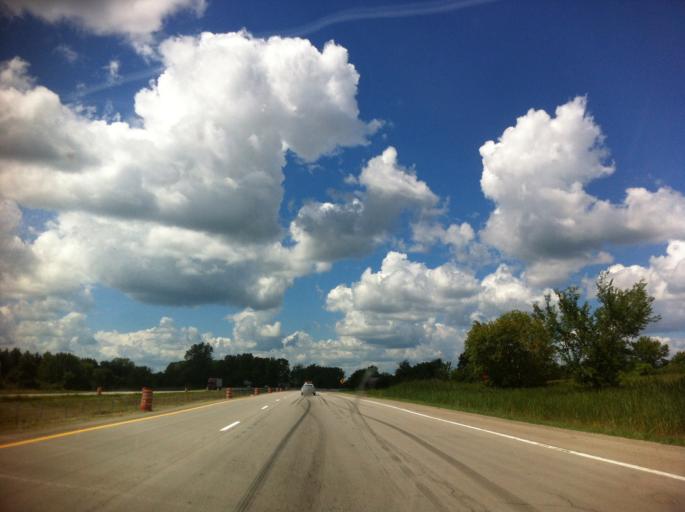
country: US
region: Michigan
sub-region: Washtenaw County
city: Milan
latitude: 42.1014
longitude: -83.6774
